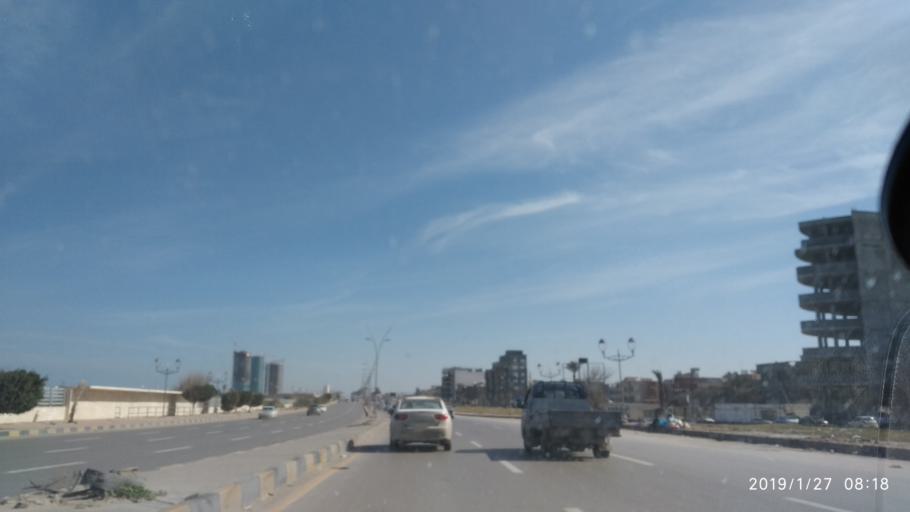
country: LY
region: Tripoli
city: Tripoli
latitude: 32.9070
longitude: 13.2493
